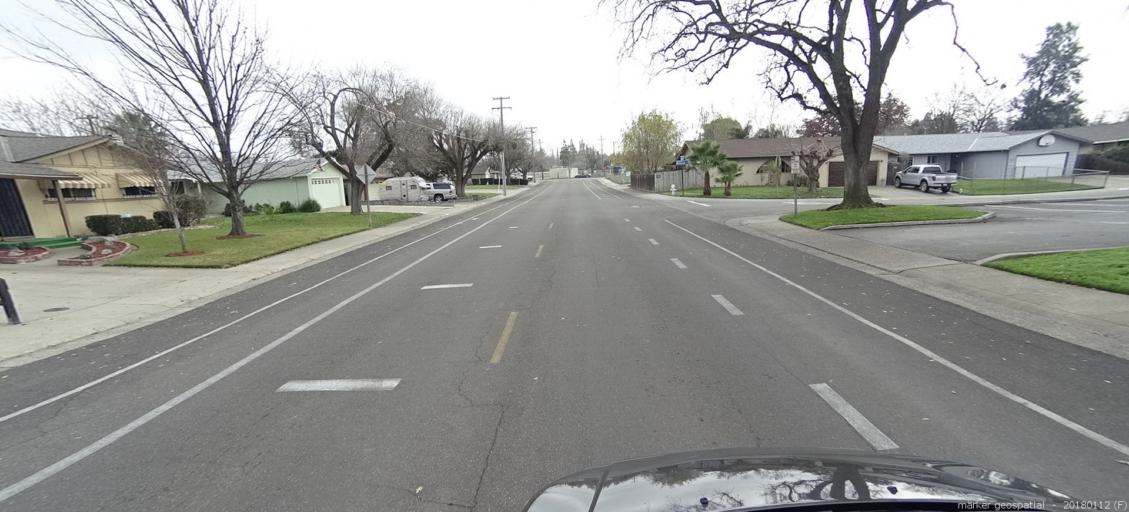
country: US
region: California
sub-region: Sacramento County
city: Rancho Cordova
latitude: 38.6053
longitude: -121.2898
